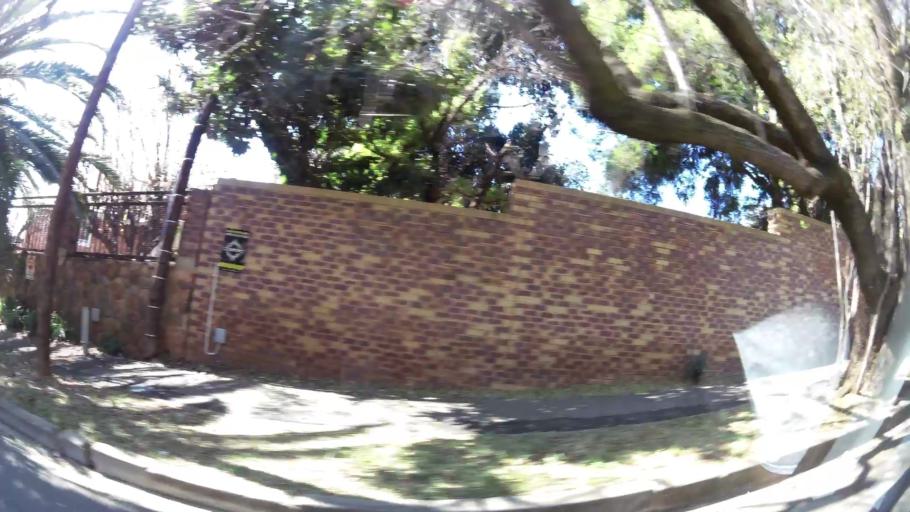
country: ZA
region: Gauteng
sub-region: City of Johannesburg Metropolitan Municipality
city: Johannesburg
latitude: -26.1648
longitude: 28.1028
